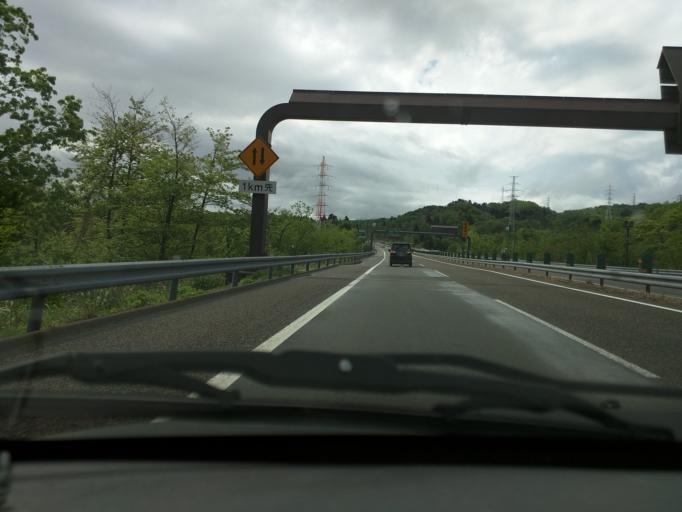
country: JP
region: Niigata
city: Joetsu
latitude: 37.1327
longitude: 138.2129
